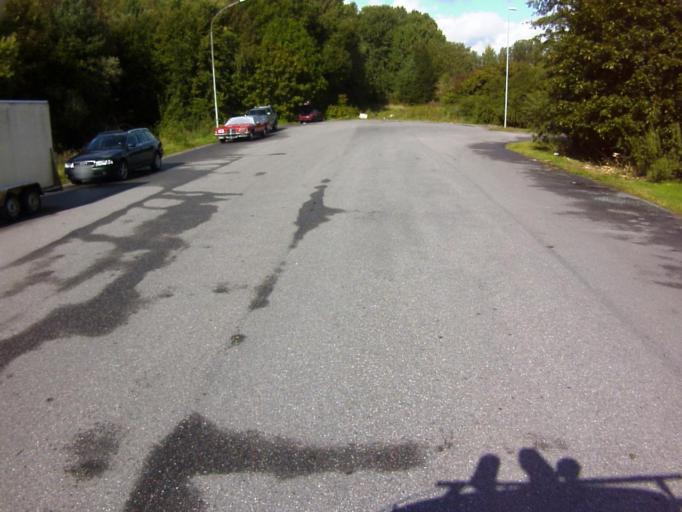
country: SE
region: Soedermanland
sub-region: Eskilstuna Kommun
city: Eskilstuna
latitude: 59.3934
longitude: 16.5282
